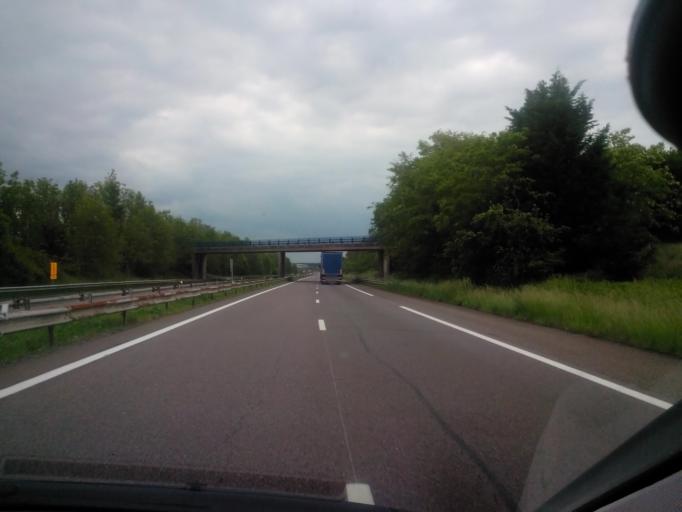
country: FR
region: Lorraine
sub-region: Departement de la Moselle
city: Seingbouse
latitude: 49.1144
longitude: 6.8449
